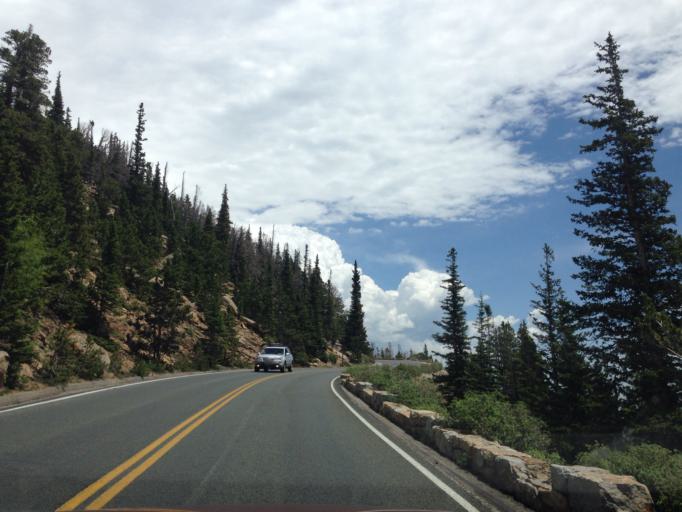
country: US
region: Colorado
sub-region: Larimer County
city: Estes Park
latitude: 40.3990
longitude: -105.6673
